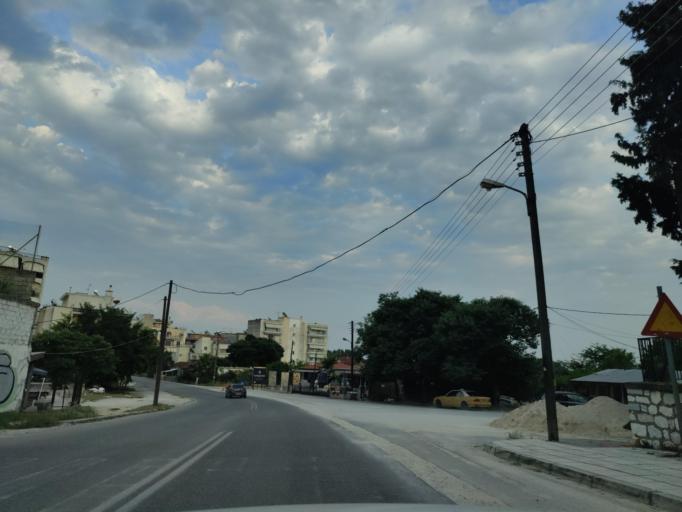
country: GR
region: East Macedonia and Thrace
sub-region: Nomos Dramas
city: Drama
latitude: 41.1502
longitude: 24.1355
